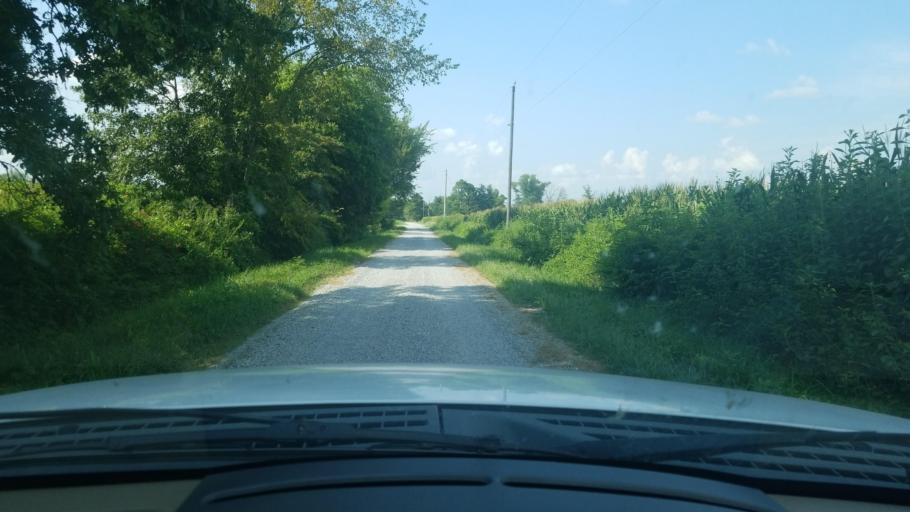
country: US
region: Illinois
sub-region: Saline County
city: Eldorado
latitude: 37.8458
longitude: -88.4802
